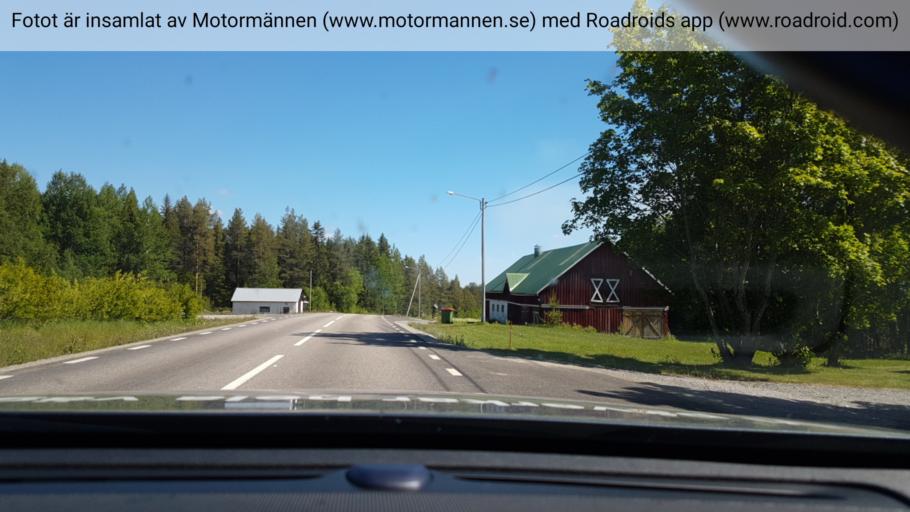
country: SE
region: Vaesterbotten
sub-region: Lycksele Kommun
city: Soderfors
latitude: 64.7098
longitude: 17.7099
